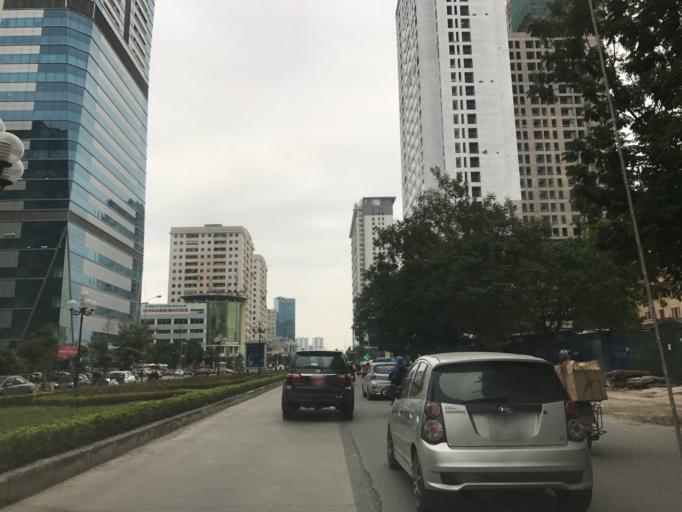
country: VN
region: Ha Noi
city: Thanh Xuan
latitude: 21.0043
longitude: 105.8033
